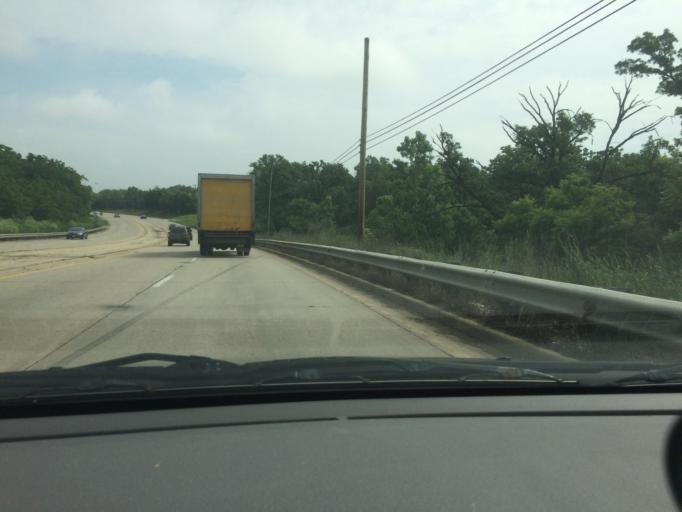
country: US
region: Illinois
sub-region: Cook County
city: Bartlett
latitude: 41.9980
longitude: -88.2046
